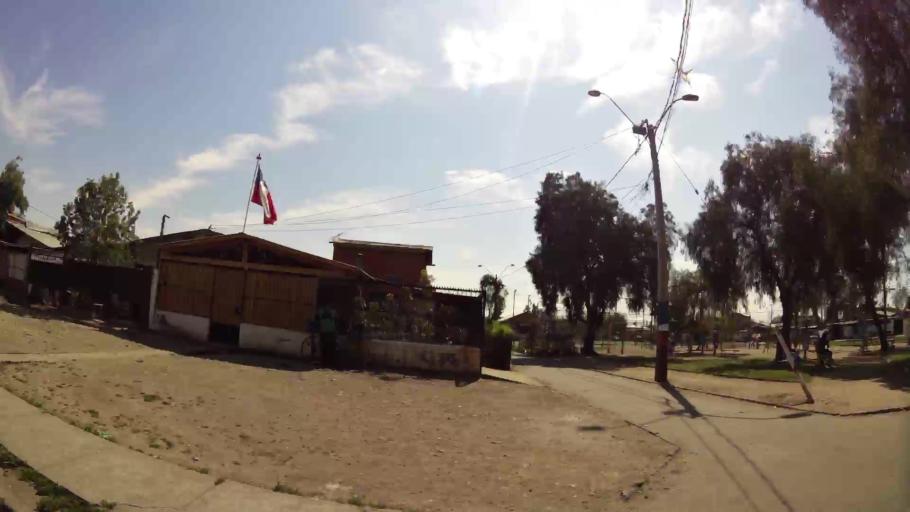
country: CL
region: Santiago Metropolitan
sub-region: Provincia de Santiago
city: La Pintana
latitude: -33.5592
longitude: -70.6385
